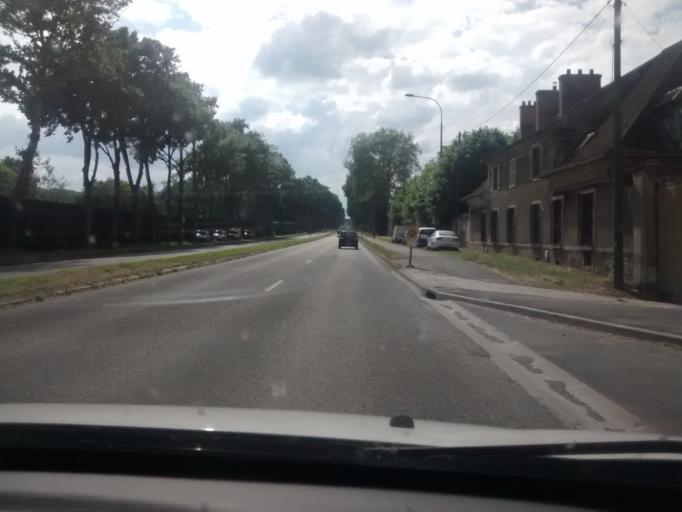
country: FR
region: Ile-de-France
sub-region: Departement des Yvelines
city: Saint-Cyr-l'Ecole
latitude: 48.8025
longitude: 2.0942
